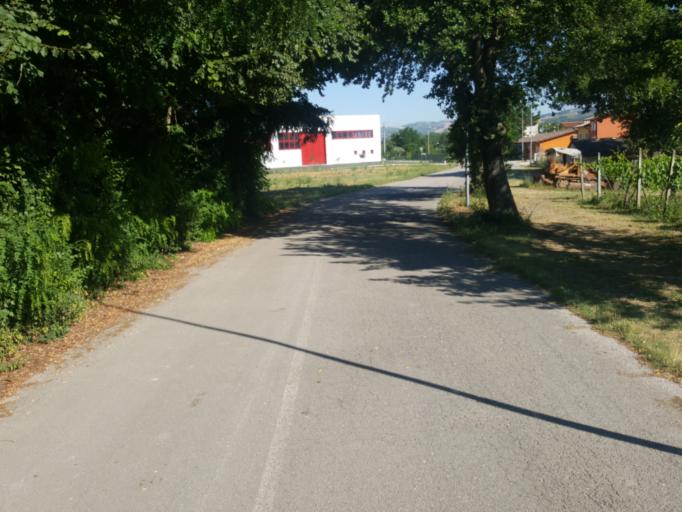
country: IT
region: The Marches
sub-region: Provincia di Pesaro e Urbino
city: Montecalvo in Foglia
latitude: 43.7846
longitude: 12.6349
